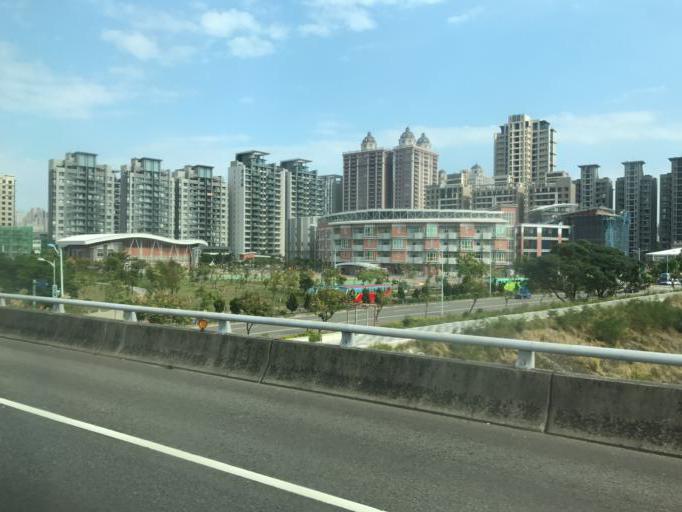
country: TW
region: Taiwan
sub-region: Hsinchu
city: Zhubei
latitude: 24.8158
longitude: 121.0128
